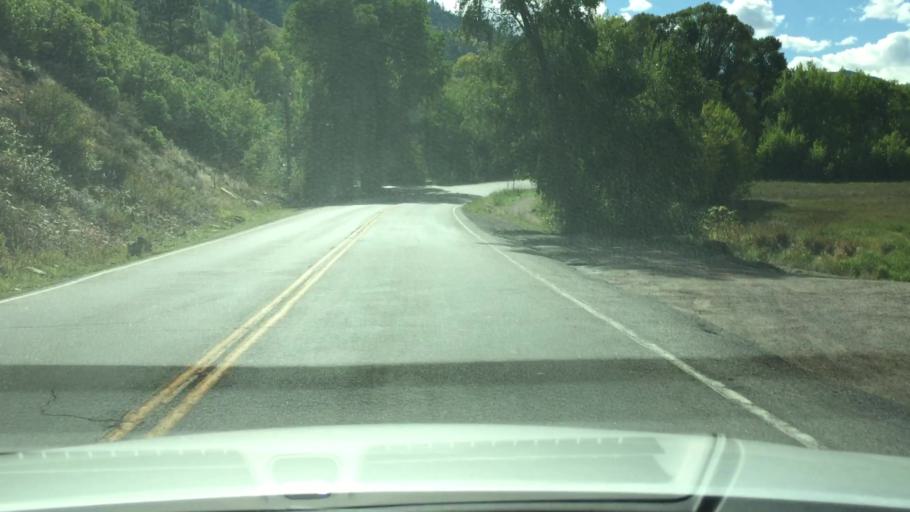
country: US
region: Colorado
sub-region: Pitkin County
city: Aspen
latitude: 39.1769
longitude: -106.7960
